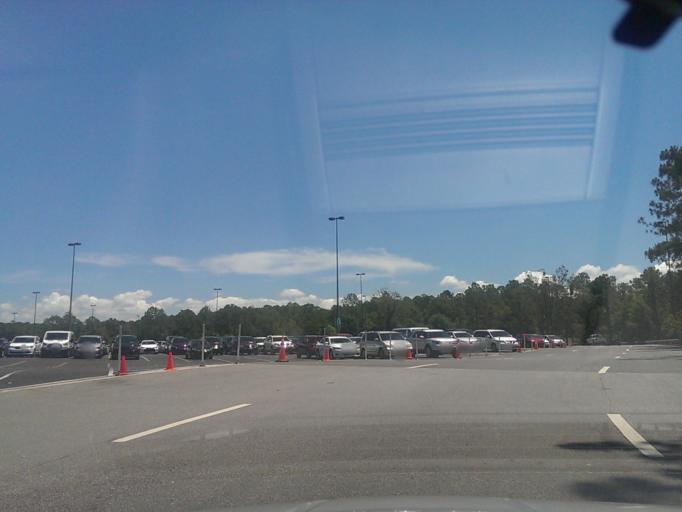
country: US
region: Florida
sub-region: Osceola County
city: Celebration
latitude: 28.3565
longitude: -81.5545
